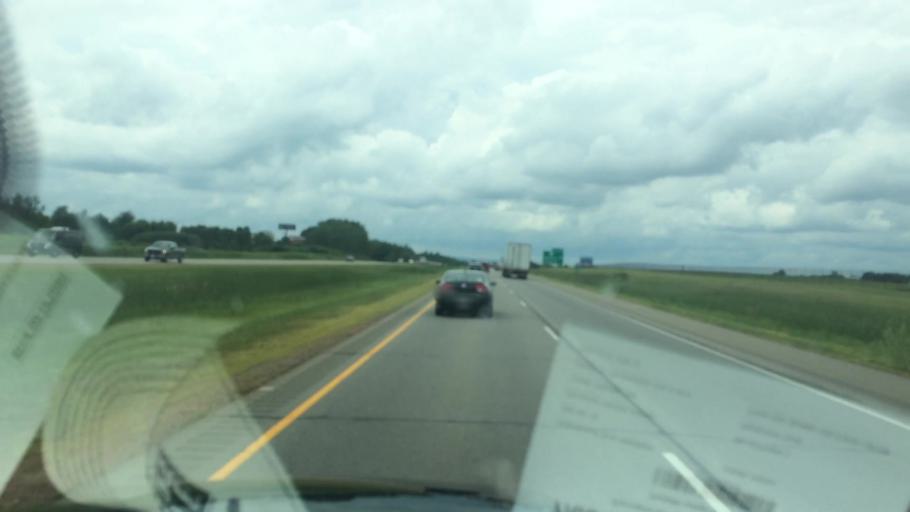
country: US
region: Wisconsin
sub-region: Marathon County
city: Mosinee
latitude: 44.7794
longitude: -89.6801
